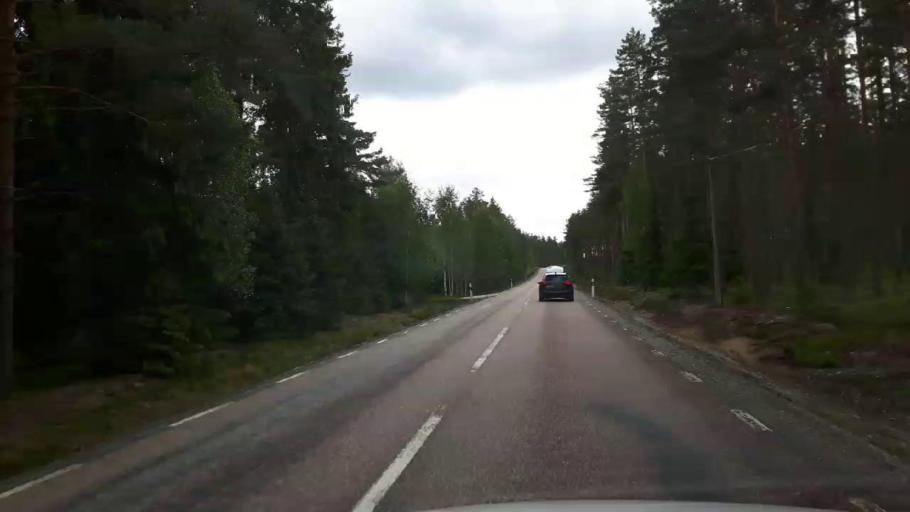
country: SE
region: Vaestmanland
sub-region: Skinnskattebergs Kommun
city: Skinnskatteberg
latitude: 59.8123
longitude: 15.8402
